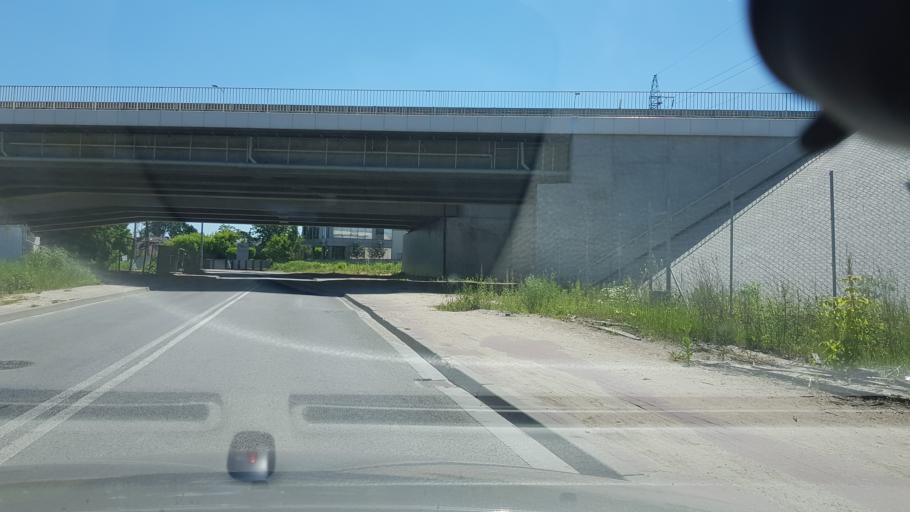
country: PL
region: Masovian Voivodeship
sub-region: Powiat wolominski
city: Marki
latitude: 52.3131
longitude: 21.1251
